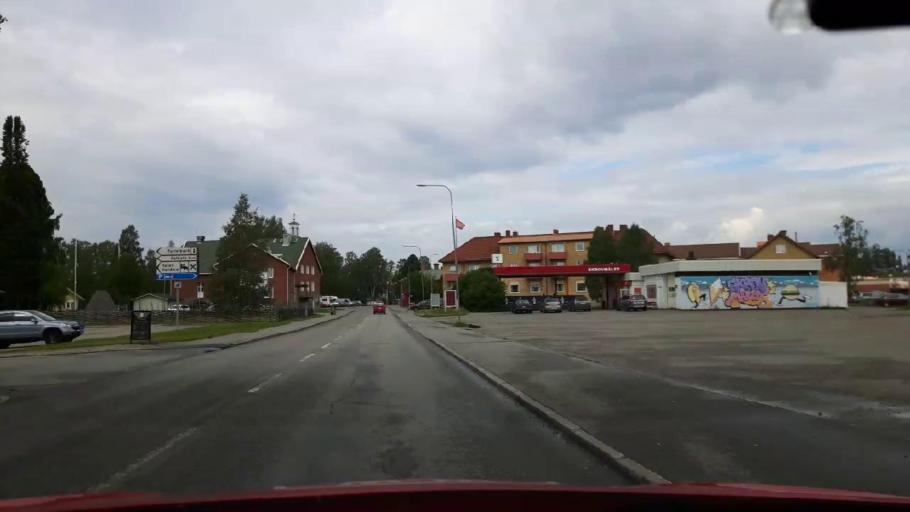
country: SE
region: Jaemtland
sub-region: Stroemsunds Kommun
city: Stroemsund
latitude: 63.8502
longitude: 15.5594
